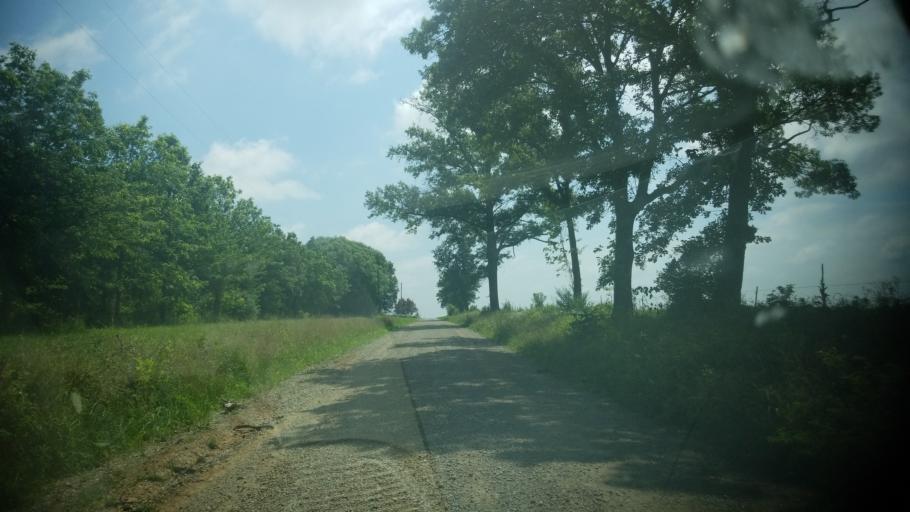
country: US
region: Illinois
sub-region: Wayne County
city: Fairfield
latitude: 38.5300
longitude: -88.3914
